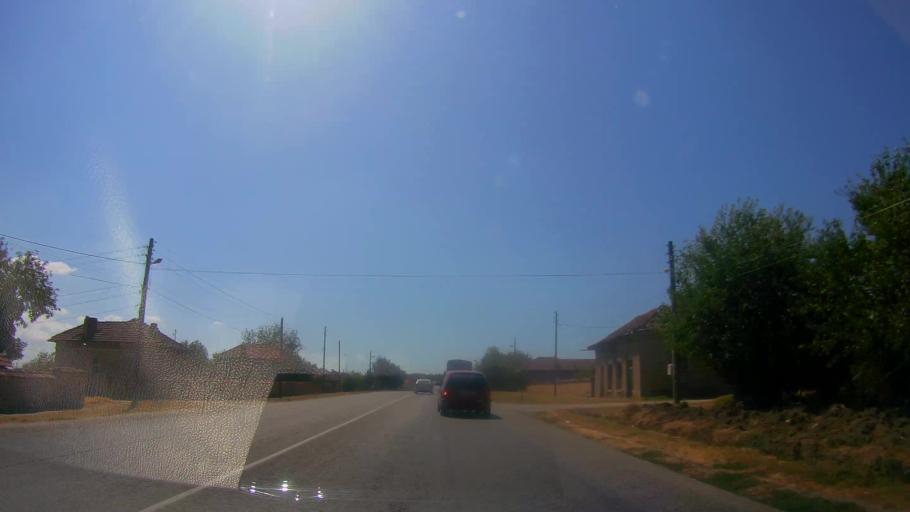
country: BG
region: Veliko Turnovo
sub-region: Obshtina Gorna Oryakhovitsa
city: Purvomaytsi
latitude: 43.2630
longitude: 25.6430
